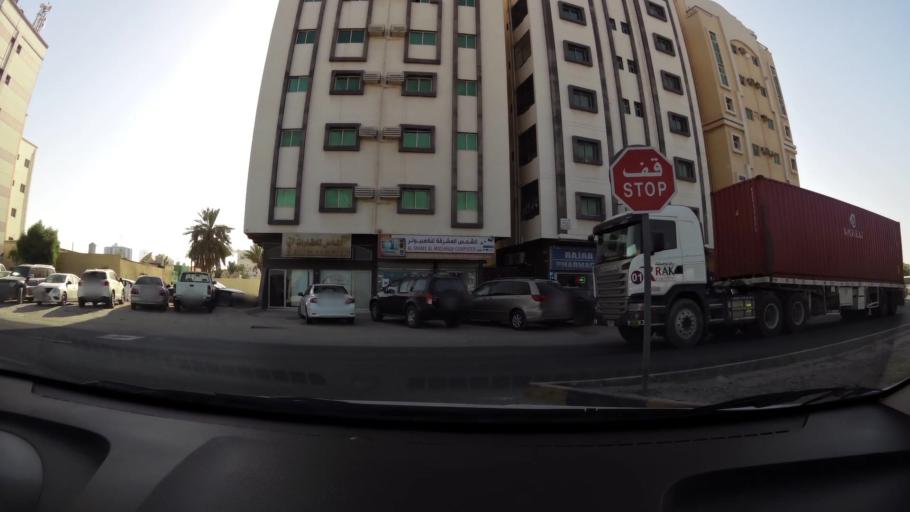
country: AE
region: Ajman
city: Ajman
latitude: 25.4127
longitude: 55.4525
